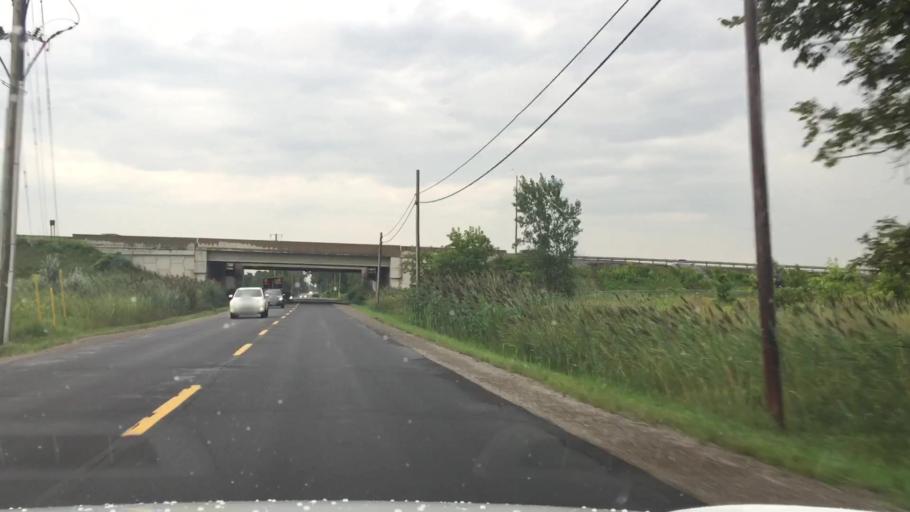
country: CA
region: Ontario
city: Markham
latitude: 43.8771
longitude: -79.2088
